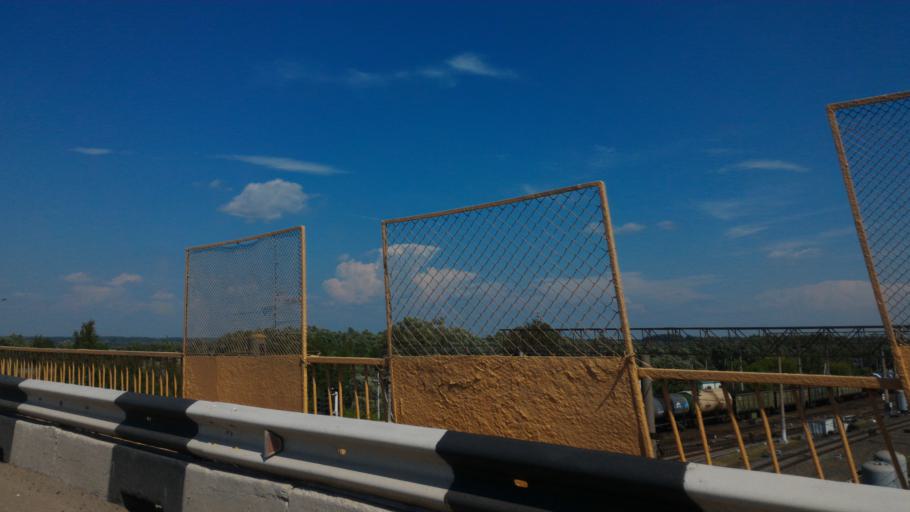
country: RU
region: Rjazan
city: Rybnoye
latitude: 54.7395
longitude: 39.4838
